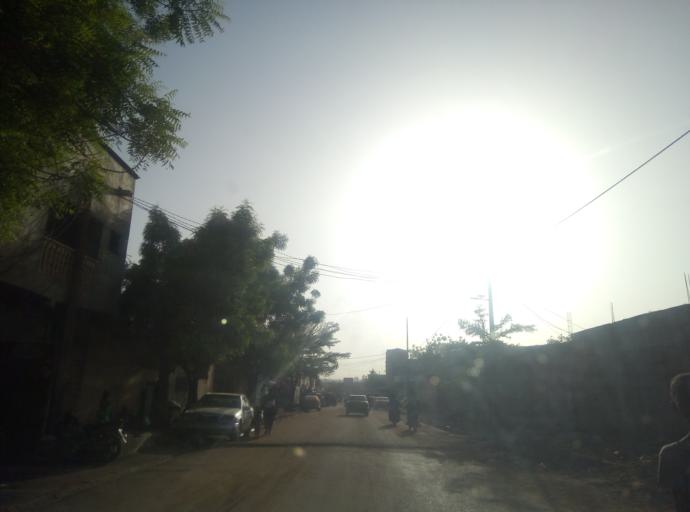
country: ML
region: Bamako
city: Bamako
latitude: 12.6031
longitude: -7.9652
